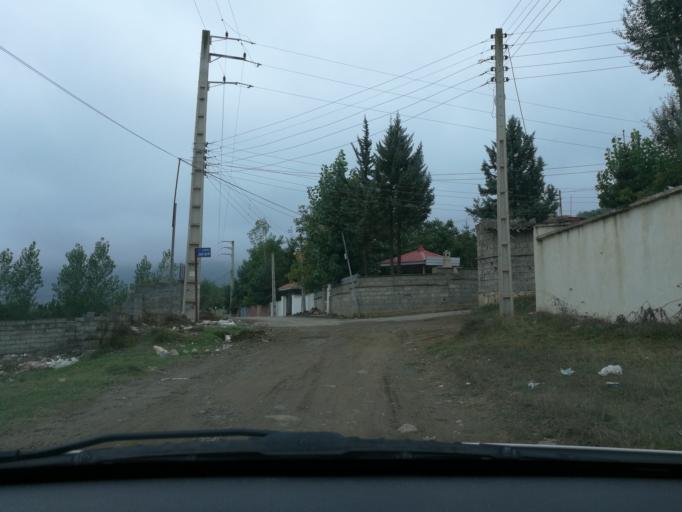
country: IR
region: Mazandaran
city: `Abbasabad
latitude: 36.5047
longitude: 51.1993
